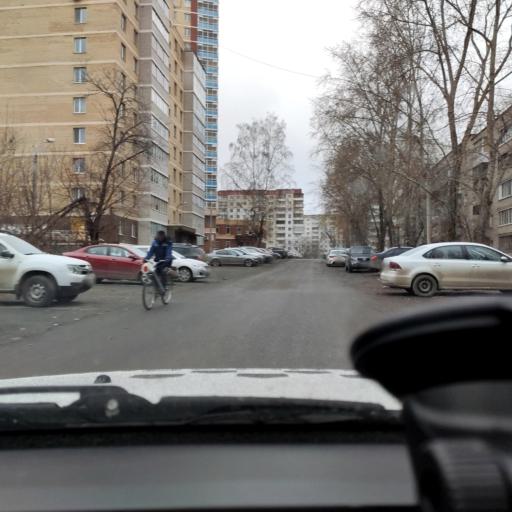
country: RU
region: Perm
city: Perm
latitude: 58.0028
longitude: 56.3080
